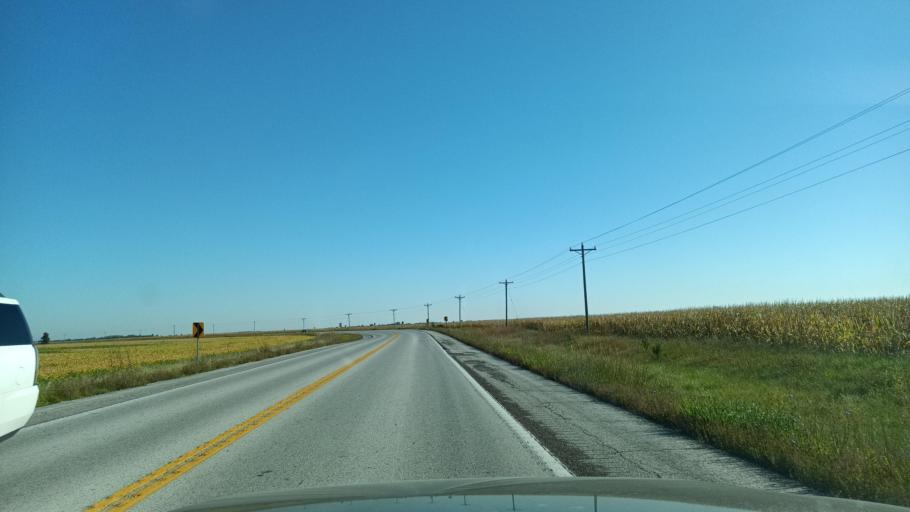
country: US
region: Missouri
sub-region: Audrain County
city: Vandalia
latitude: 39.4130
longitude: -91.6394
